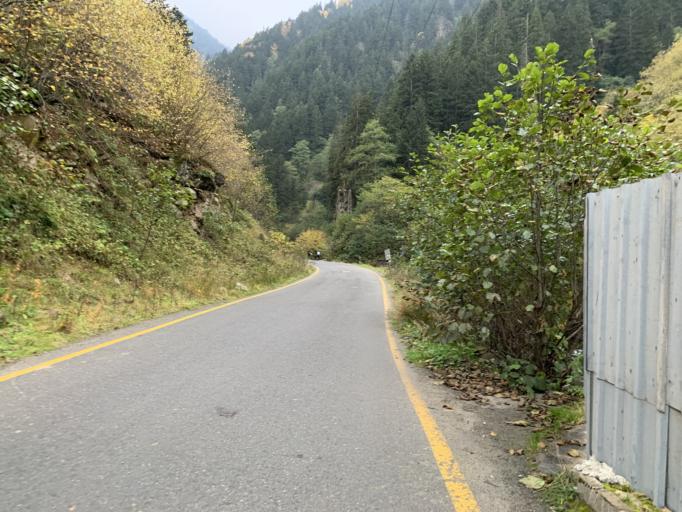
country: TR
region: Trabzon
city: Uzungol
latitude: 40.5937
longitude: 40.3210
